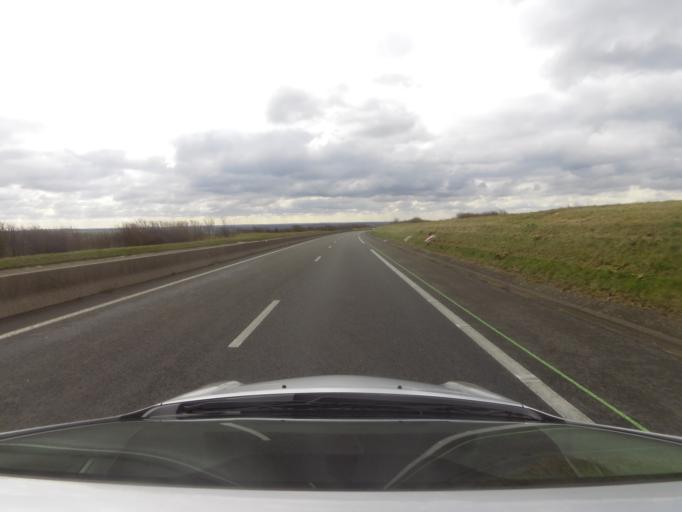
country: FR
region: Nord-Pas-de-Calais
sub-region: Departement du Pas-de-Calais
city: Etaples
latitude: 50.5466
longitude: 1.6762
